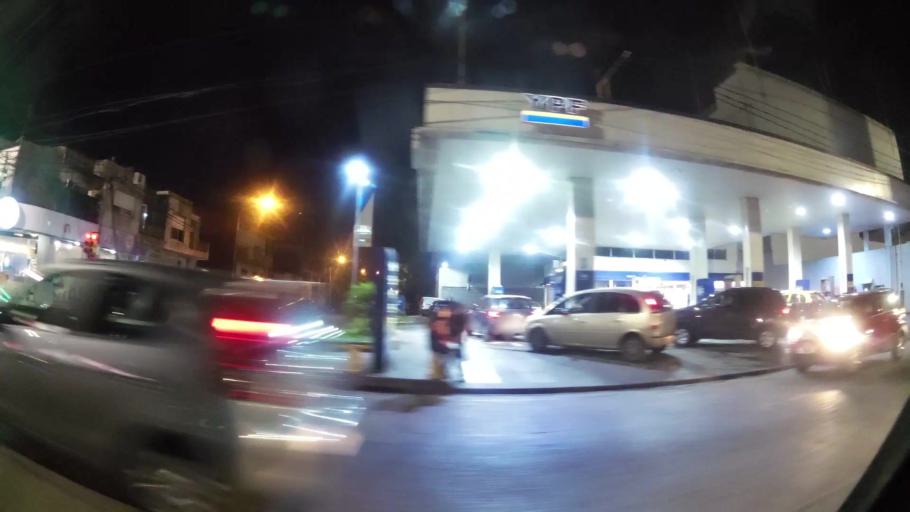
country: AR
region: Buenos Aires
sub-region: Partido de Lanus
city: Lanus
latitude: -34.7179
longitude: -58.3576
